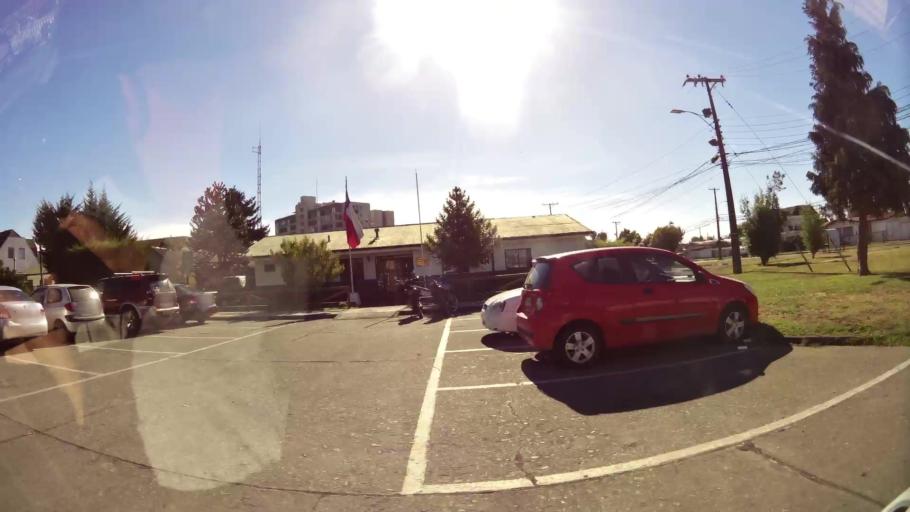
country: CL
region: Biobio
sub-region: Provincia de Concepcion
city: Concepcion
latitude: -36.8423
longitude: -73.1130
